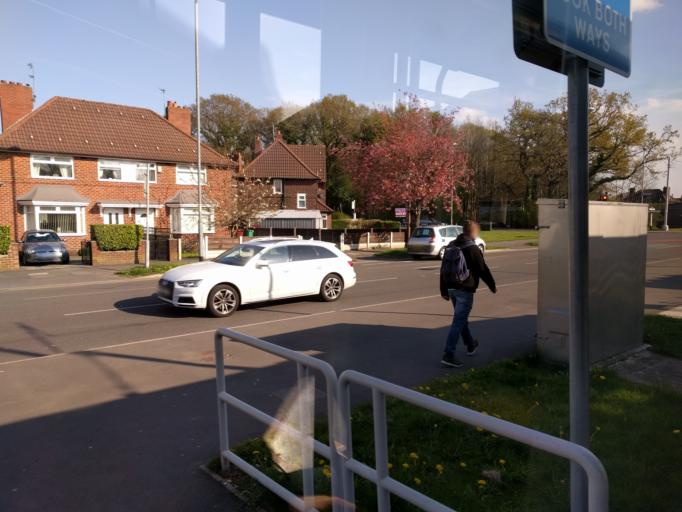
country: GB
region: England
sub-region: Manchester
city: Didsbury
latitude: 53.3829
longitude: -2.2562
